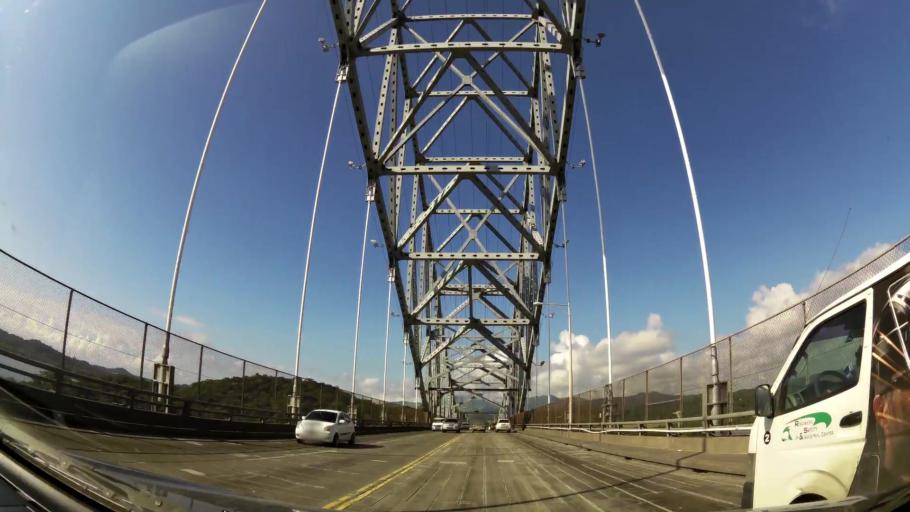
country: PA
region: Panama
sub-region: Distrito de Panama
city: Ancon
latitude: 8.9430
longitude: -79.5654
